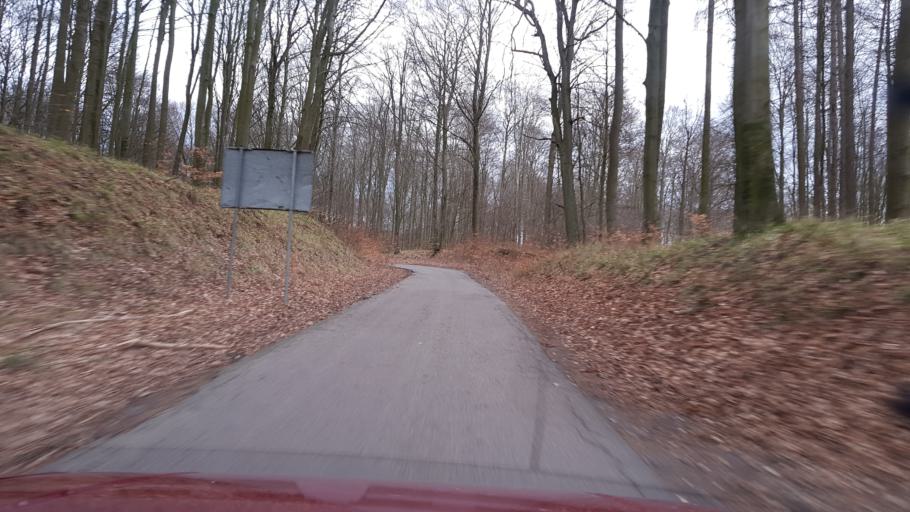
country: PL
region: West Pomeranian Voivodeship
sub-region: Szczecin
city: Szczecin
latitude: 53.3350
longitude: 14.6463
